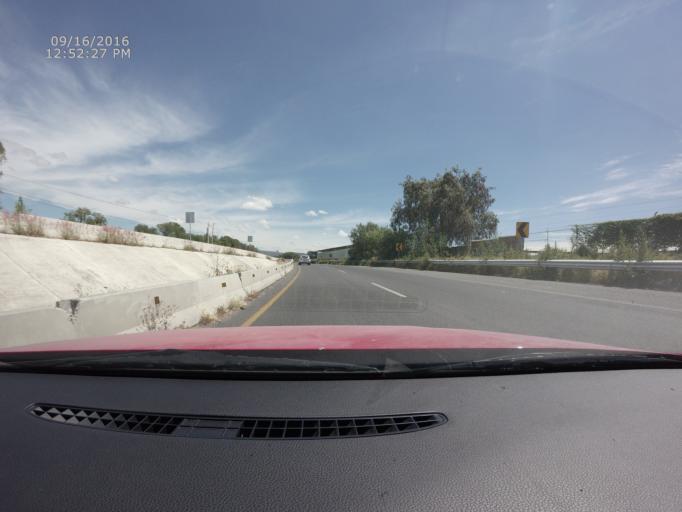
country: MX
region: Queretaro
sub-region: Colon
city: Purisima de Cubos (La Purisima)
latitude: 20.6161
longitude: -100.1421
